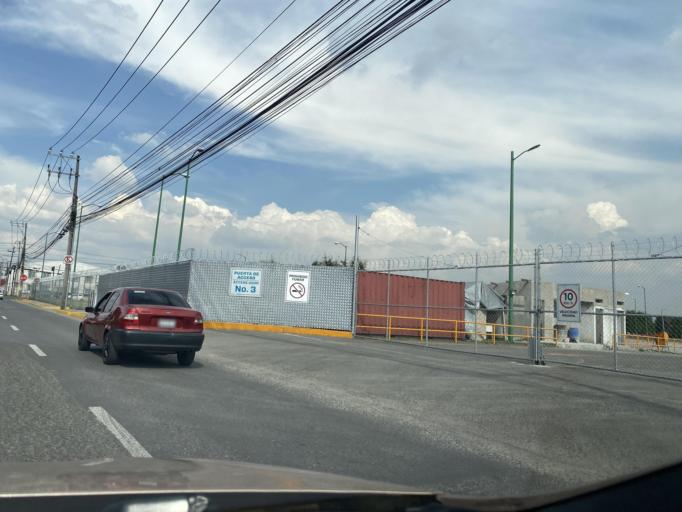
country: IN
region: Karnataka
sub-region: Dakshina Kannada
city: Puttur
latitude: 12.7366
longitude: 75.1836
